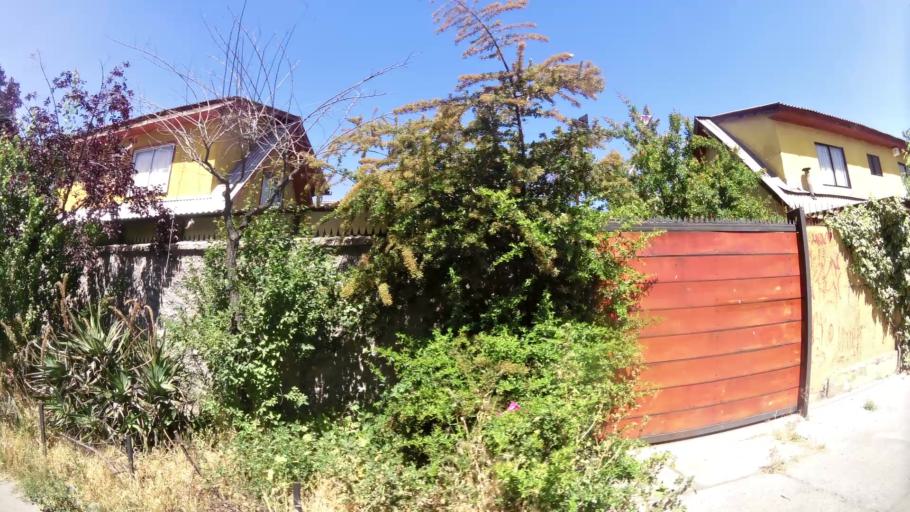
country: CL
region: Santiago Metropolitan
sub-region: Provincia de Maipo
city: San Bernardo
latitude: -33.5763
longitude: -70.6876
